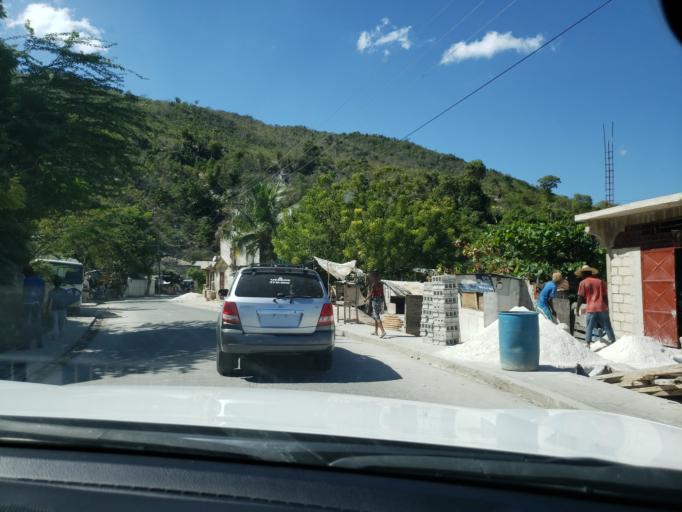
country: HT
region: Nippes
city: Miragoane
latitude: 18.4438
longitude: -73.0972
